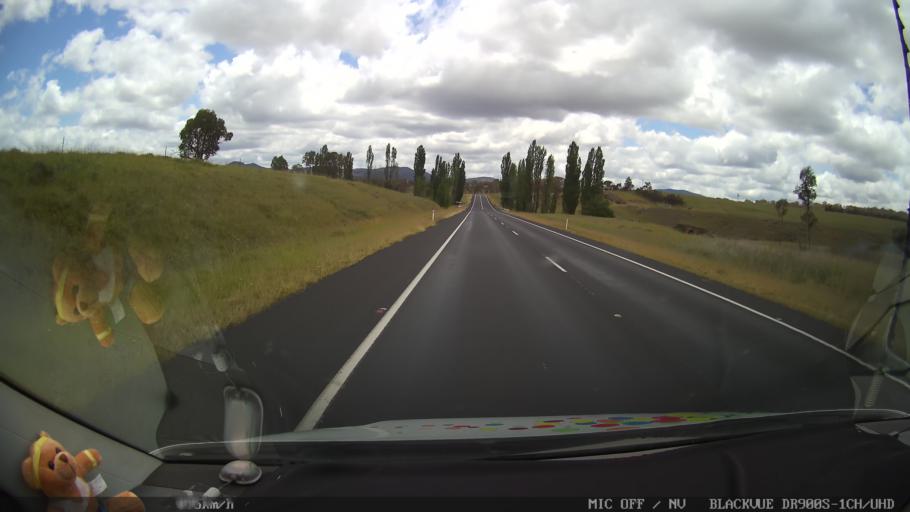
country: AU
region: New South Wales
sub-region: Glen Innes Severn
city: Glen Innes
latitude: -29.3905
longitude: 151.8848
